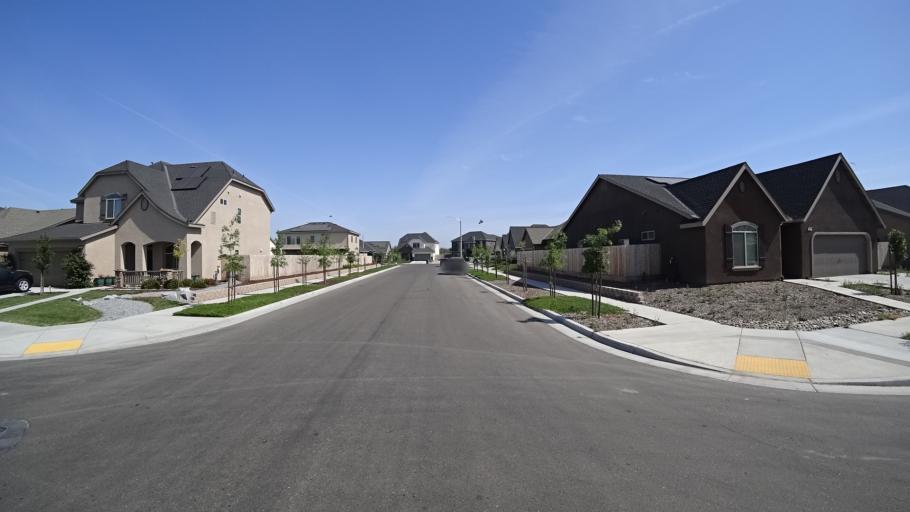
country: US
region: California
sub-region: Kings County
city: Hanford
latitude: 36.3378
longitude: -119.6793
